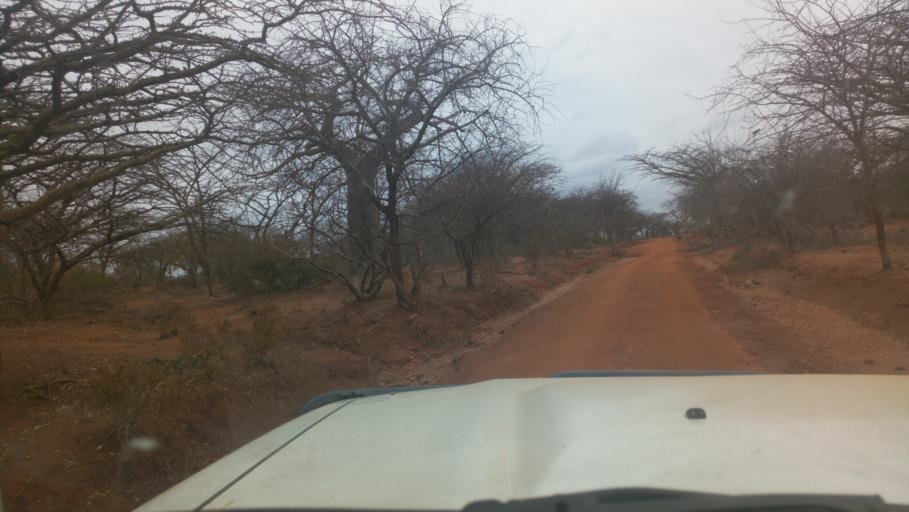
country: KE
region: Makueni
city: Makueni
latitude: -2.0151
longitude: 38.0740
